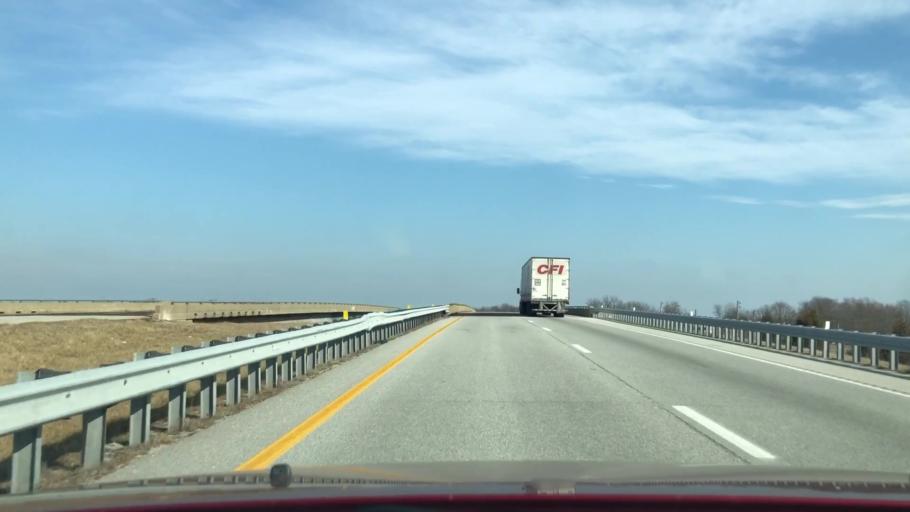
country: US
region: Missouri
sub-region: Webster County
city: Rogersville
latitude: 37.1573
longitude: -92.9334
